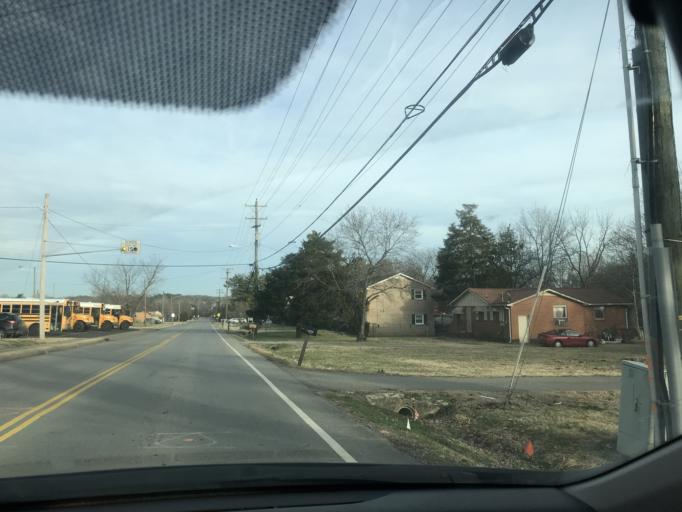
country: US
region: Tennessee
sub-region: Davidson County
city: Nashville
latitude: 36.2196
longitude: -86.8284
